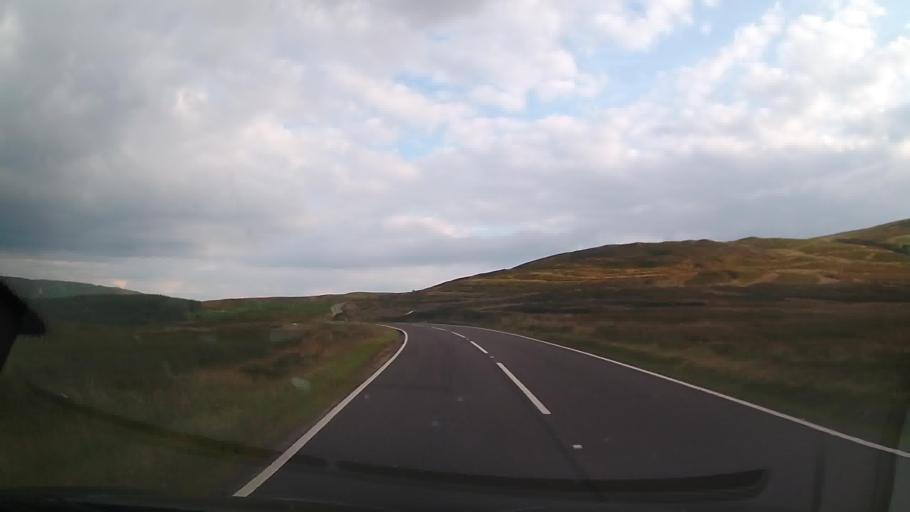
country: GB
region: Wales
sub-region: Denbighshire
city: Llandrillo
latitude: 52.8785
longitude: -3.4790
